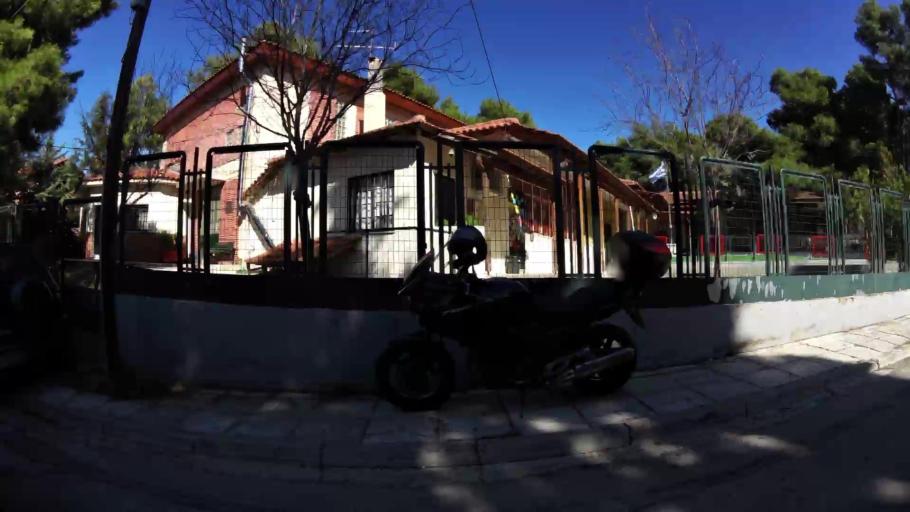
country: GR
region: Attica
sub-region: Nomarchia Athinas
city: Ekali
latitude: 38.1107
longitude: 23.8371
